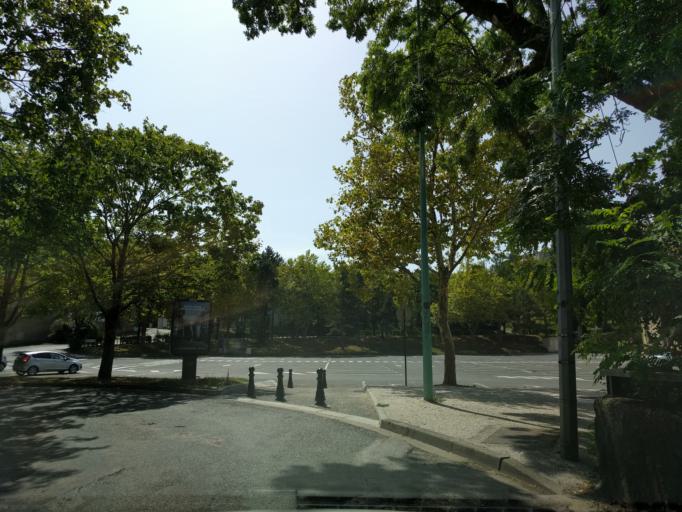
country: FR
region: Midi-Pyrenees
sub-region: Departement du Tarn
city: Castres
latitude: 43.6017
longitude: 2.2499
